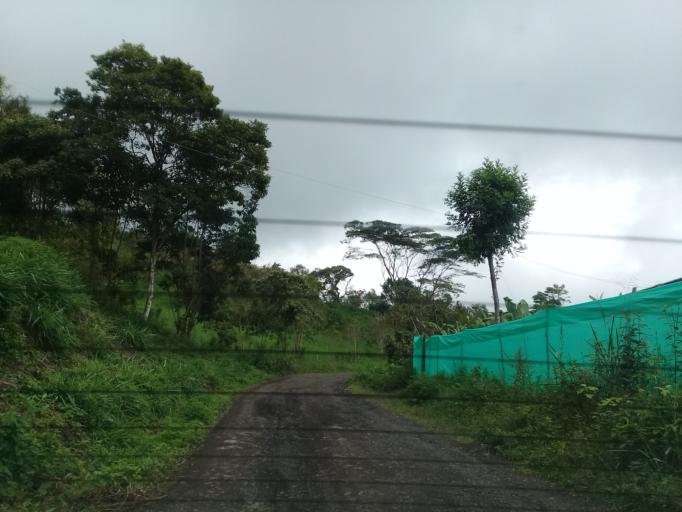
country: CO
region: Cundinamarca
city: Quipile
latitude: 4.7208
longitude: -74.5519
